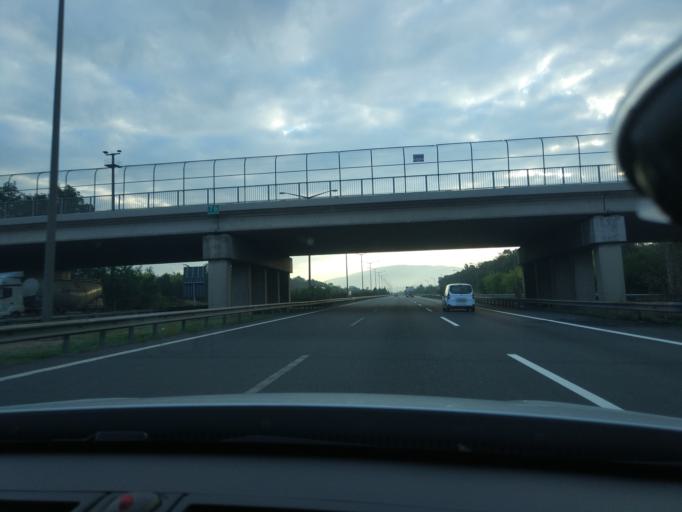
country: TR
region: Sakarya
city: Hendek
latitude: 40.7536
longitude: 30.7176
